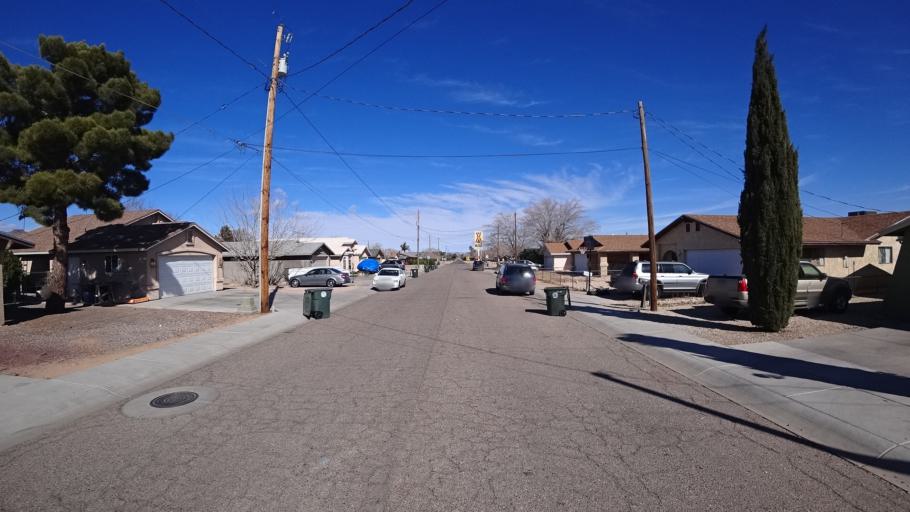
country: US
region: Arizona
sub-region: Mohave County
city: New Kingman-Butler
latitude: 35.2309
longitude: -114.0183
